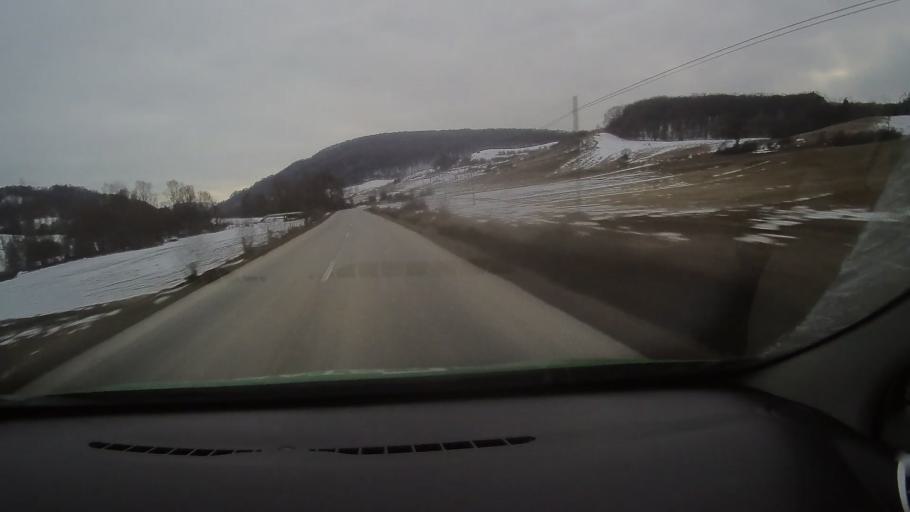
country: RO
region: Harghita
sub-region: Comuna Mugeni
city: Mugeni
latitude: 46.2309
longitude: 25.2405
